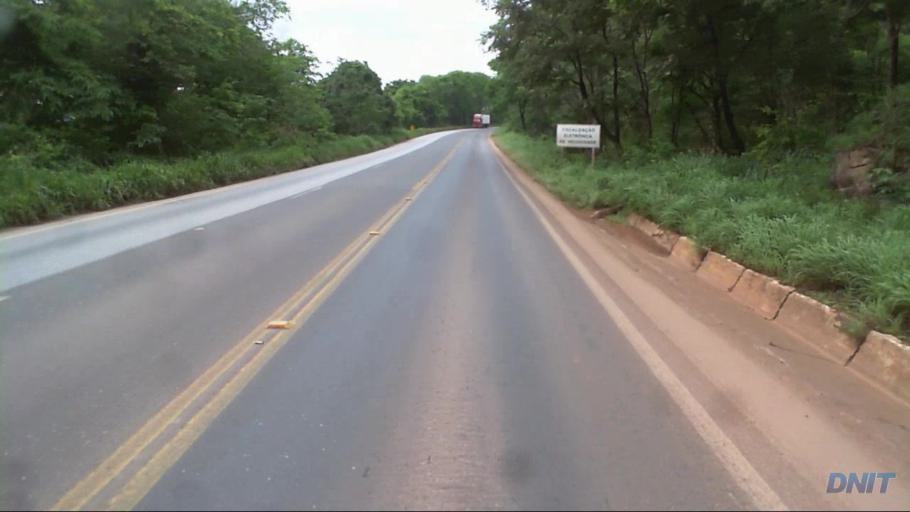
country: BR
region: Goias
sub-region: Uruacu
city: Uruacu
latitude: -14.5690
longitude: -49.1563
